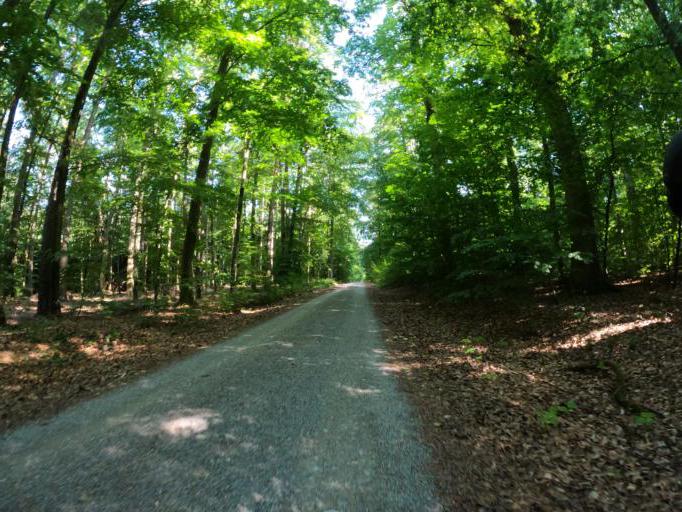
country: DE
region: Baden-Wuerttemberg
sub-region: Regierungsbezirk Stuttgart
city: Leonberg
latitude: 48.7675
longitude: 9.0145
